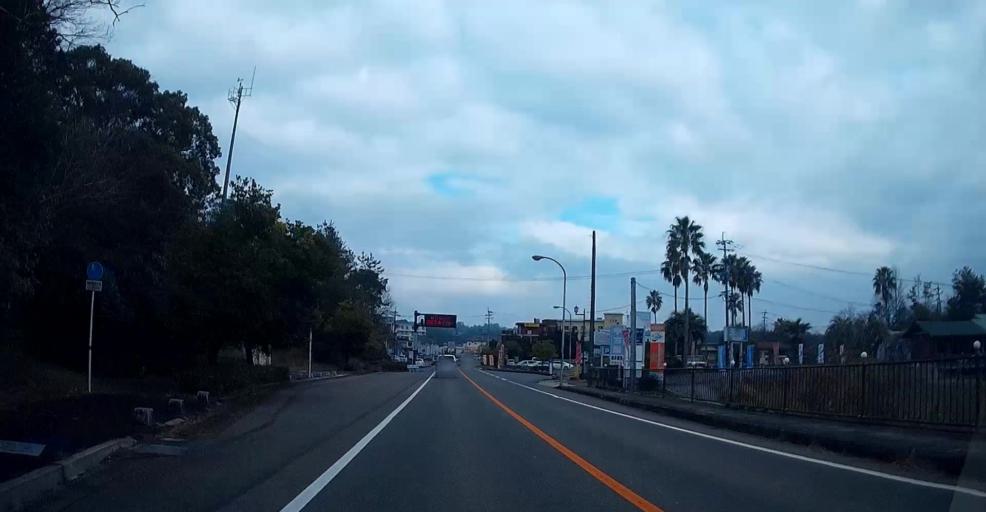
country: JP
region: Kumamoto
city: Yatsushiro
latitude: 32.5471
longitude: 130.4221
